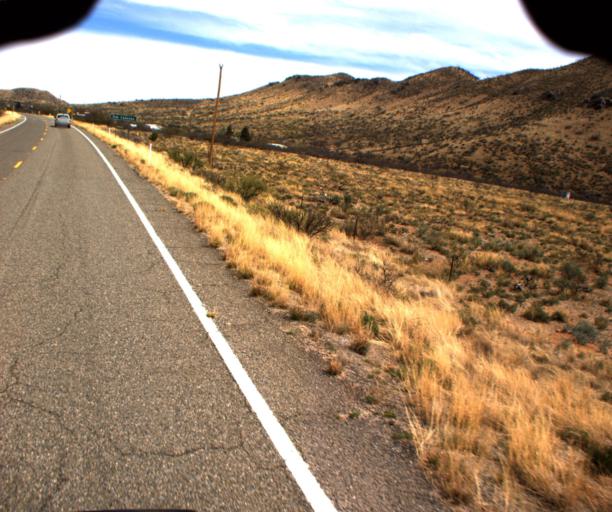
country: US
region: Arizona
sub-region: Cochise County
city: Willcox
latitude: 32.1760
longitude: -109.6212
